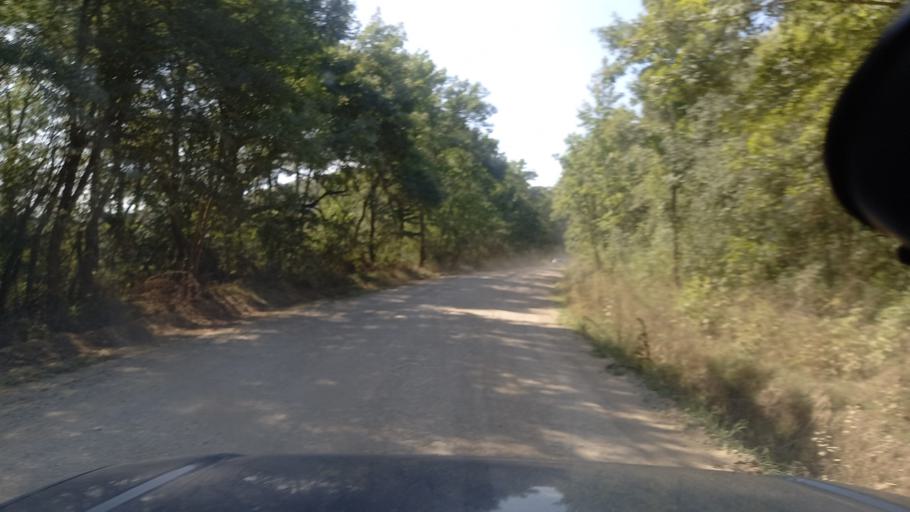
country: RU
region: Krasnodarskiy
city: Azovskaya
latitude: 44.6947
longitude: 38.6433
